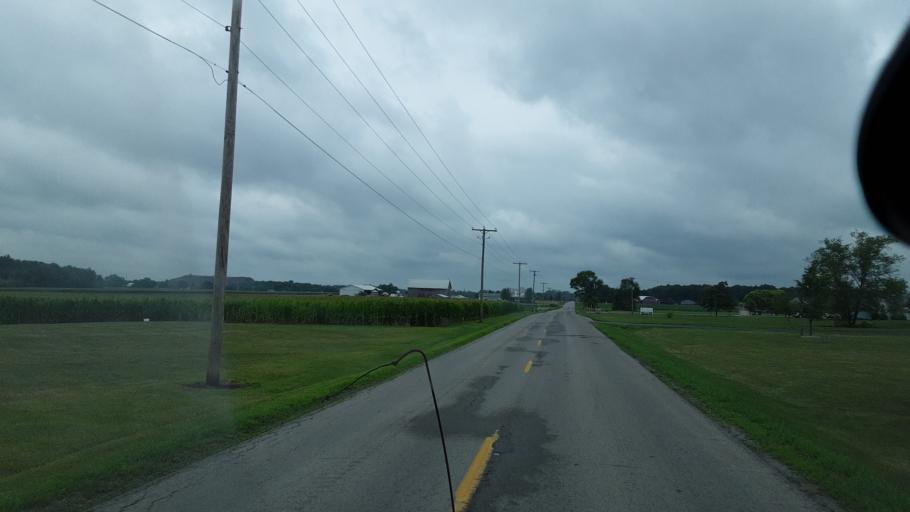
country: US
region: Indiana
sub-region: Allen County
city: New Haven
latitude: 40.9472
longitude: -85.0341
